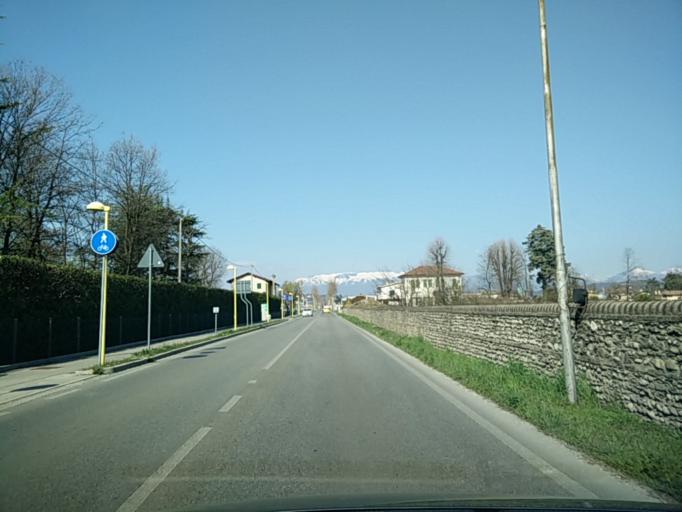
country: IT
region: Veneto
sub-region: Provincia di Treviso
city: Priula-Colfosco
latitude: 45.8124
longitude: 12.2337
